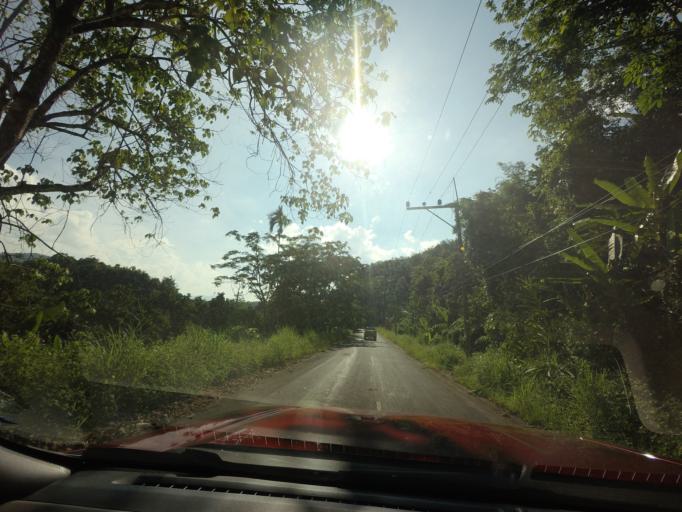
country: TH
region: Yala
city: Than To
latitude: 6.0812
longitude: 101.3315
